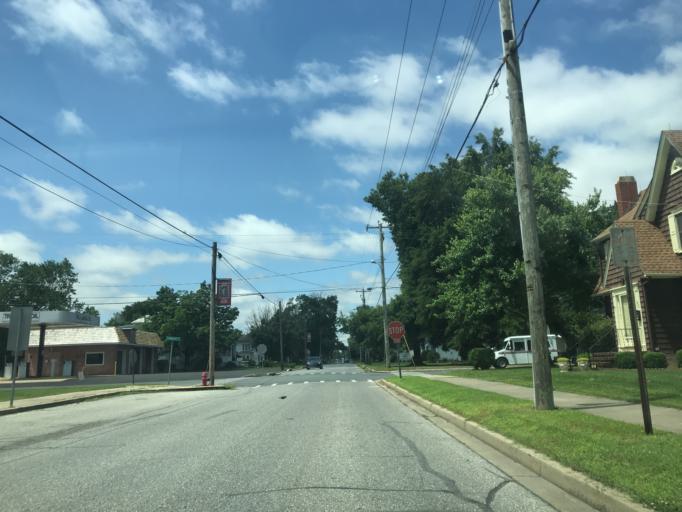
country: US
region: Maryland
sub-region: Caroline County
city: Federalsburg
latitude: 38.6911
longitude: -75.7799
